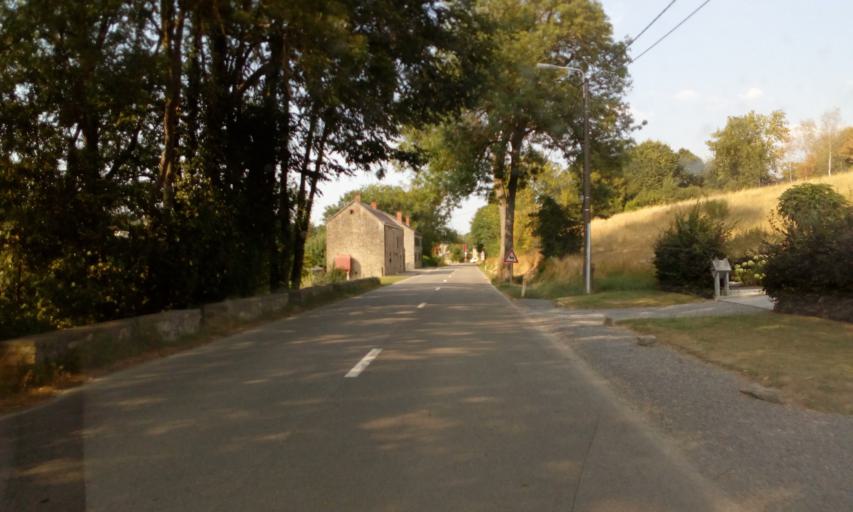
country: BE
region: Wallonia
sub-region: Province du Luxembourg
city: Tellin
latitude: 50.1176
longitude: 5.2470
